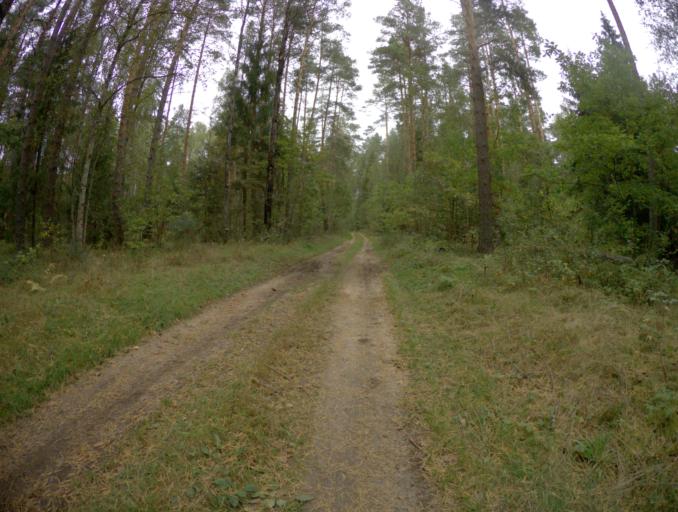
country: RU
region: Vladimir
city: Bogolyubovo
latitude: 56.1370
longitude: 40.5393
